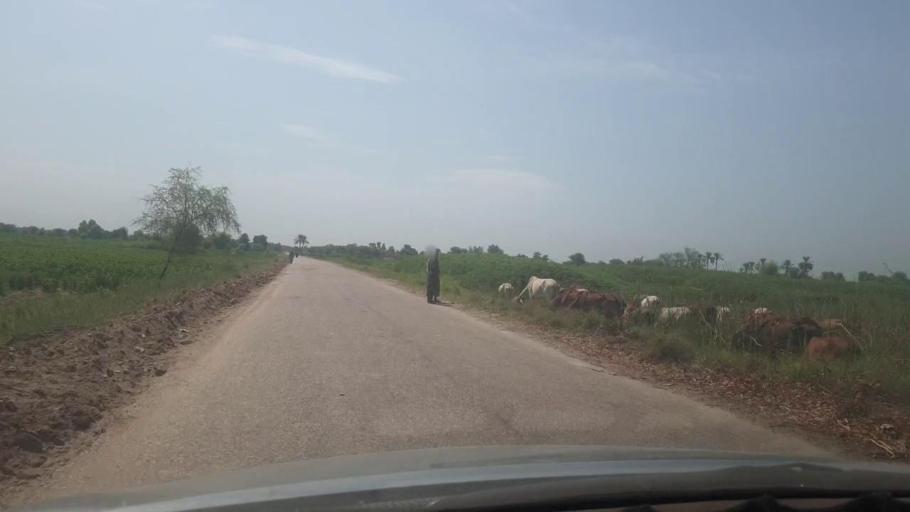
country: PK
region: Sindh
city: Bozdar
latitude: 27.2169
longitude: 68.5703
